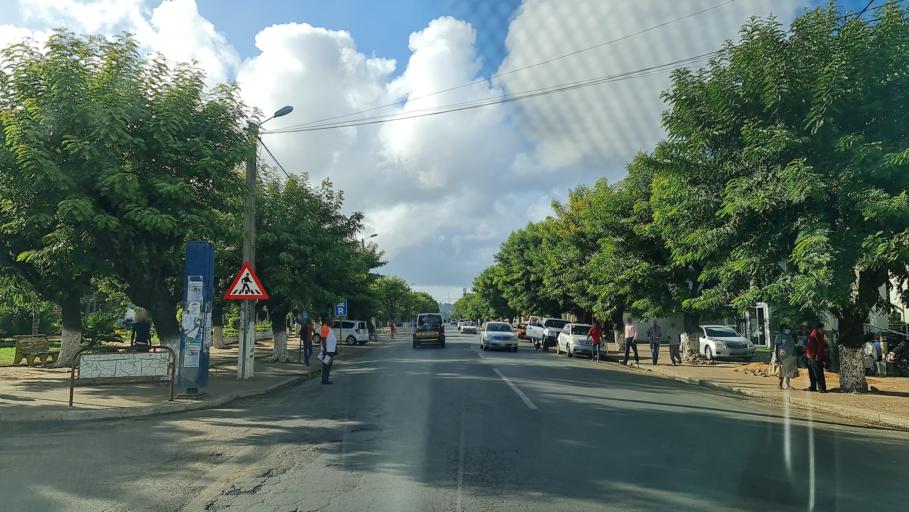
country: MZ
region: Gaza
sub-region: Xai-Xai District
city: Xai-Xai
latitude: -25.0411
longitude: 33.6407
